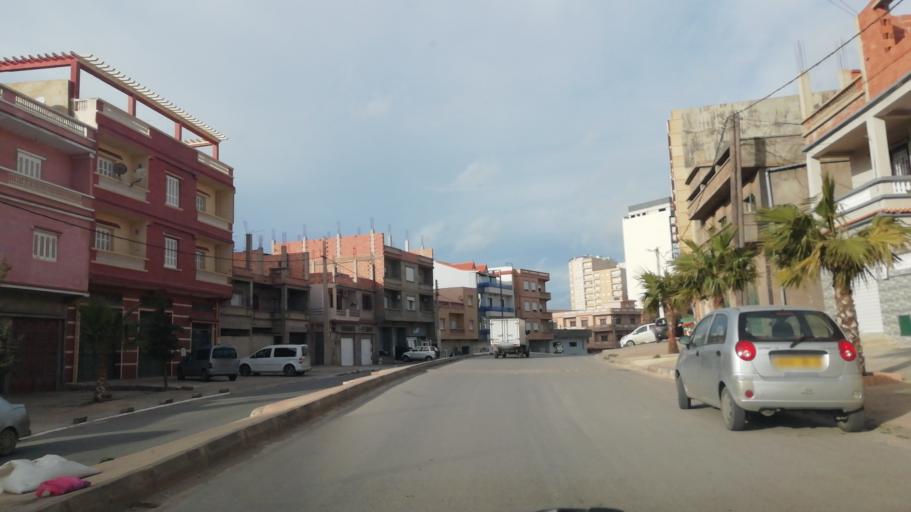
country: DZ
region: Oran
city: Bir el Djir
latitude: 35.7348
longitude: -0.5725
